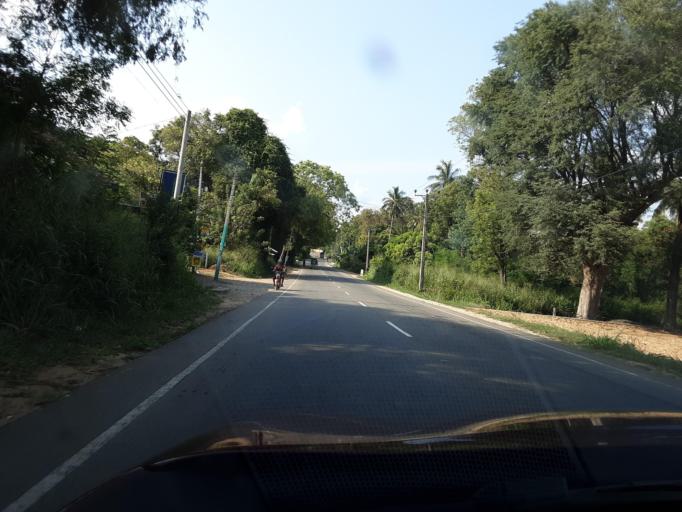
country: LK
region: Uva
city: Haputale
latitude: 6.5925
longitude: 81.1419
